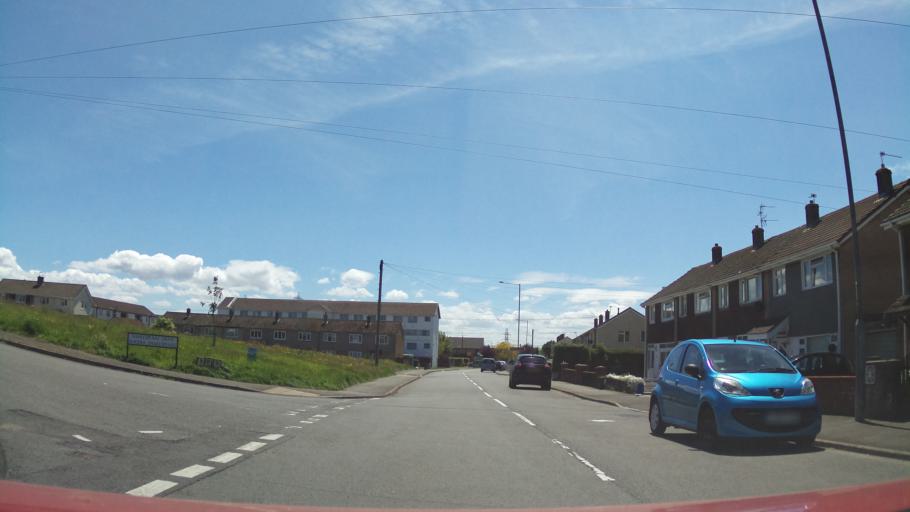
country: GB
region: Wales
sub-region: Monmouthshire
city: Caldicot
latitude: 51.5883
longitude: -2.7639
